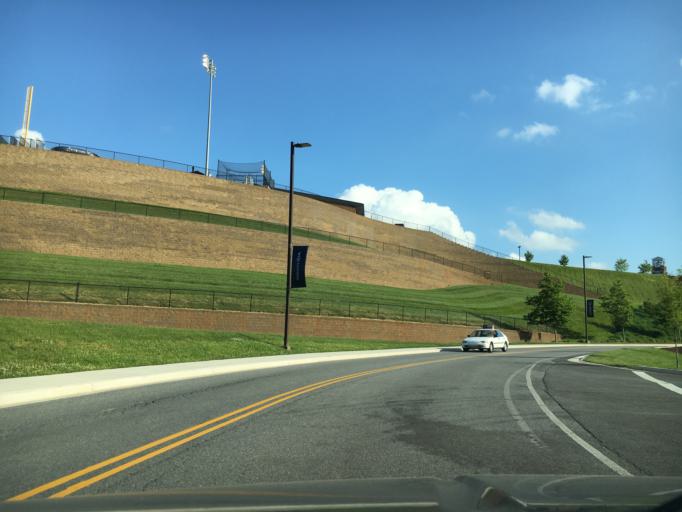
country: US
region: Virginia
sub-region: City of Lynchburg
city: West Lynchburg
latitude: 37.3576
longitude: -79.1782
